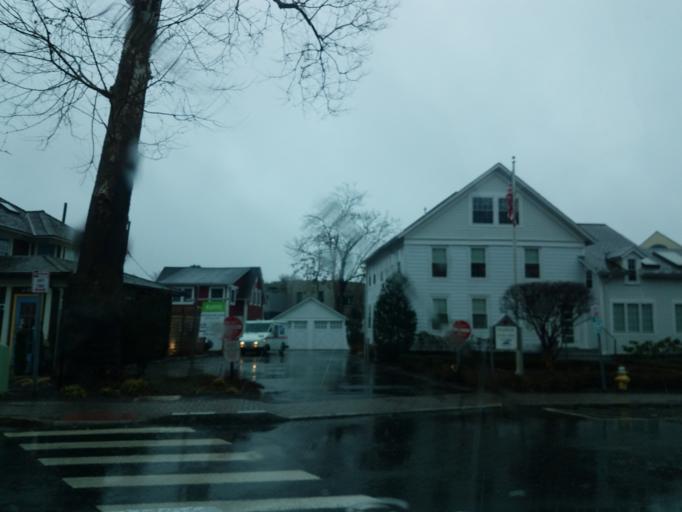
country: US
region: Connecticut
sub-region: Fairfield County
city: Westport
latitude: 41.1424
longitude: -73.3601
